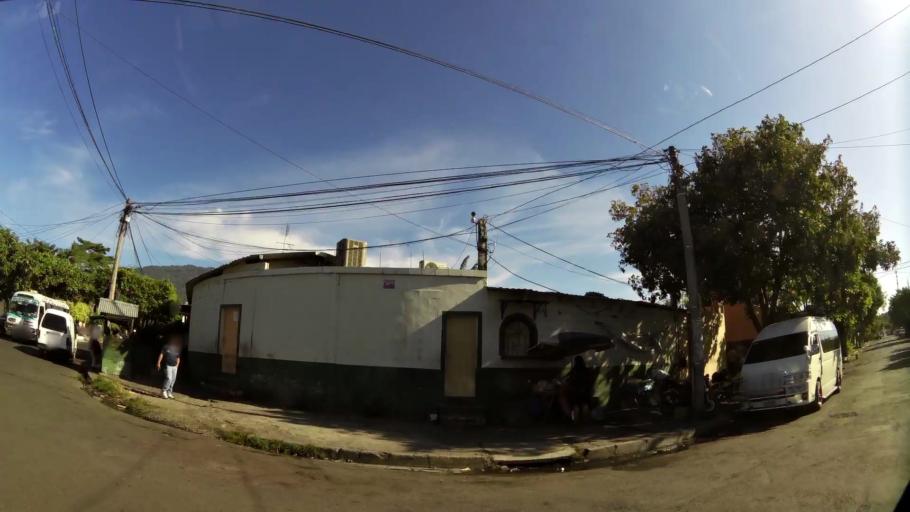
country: SV
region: La Libertad
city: Santa Tecla
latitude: 13.6874
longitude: -89.2942
